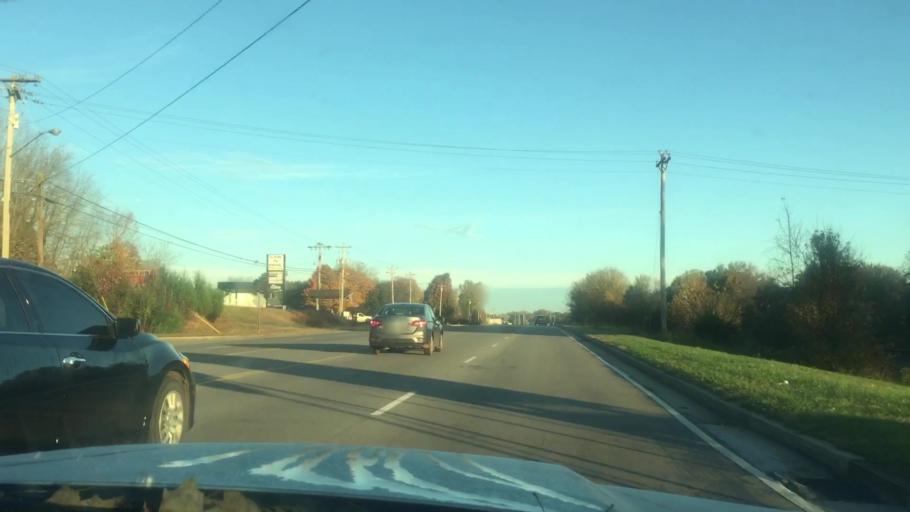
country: US
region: Tennessee
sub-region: Franklin County
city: Estill Springs
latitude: 35.2638
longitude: -86.1233
